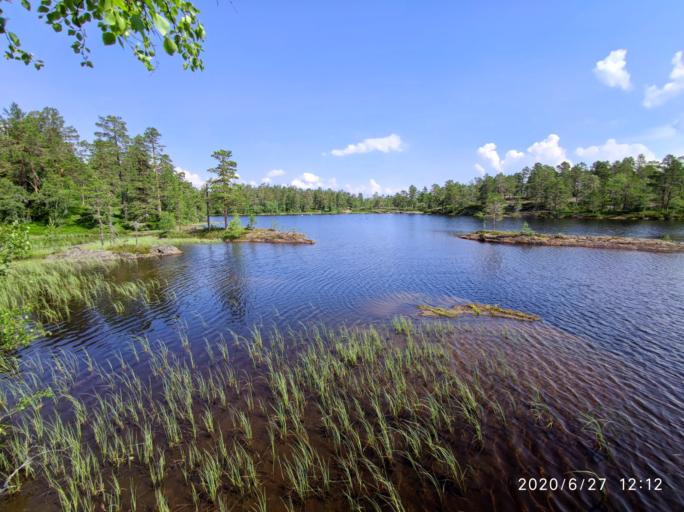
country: NO
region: Buskerud
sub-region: Kongsberg
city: Kongsberg
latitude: 59.6547
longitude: 9.5909
